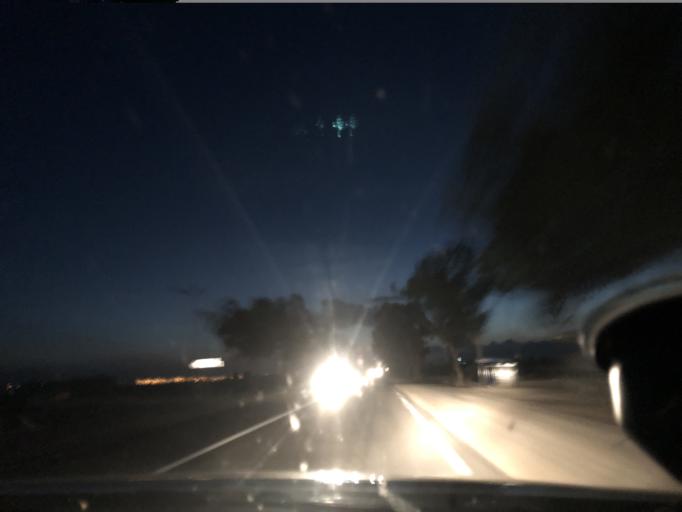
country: TN
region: Al Qasrayn
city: Kasserine
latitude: 35.2214
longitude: 8.9325
